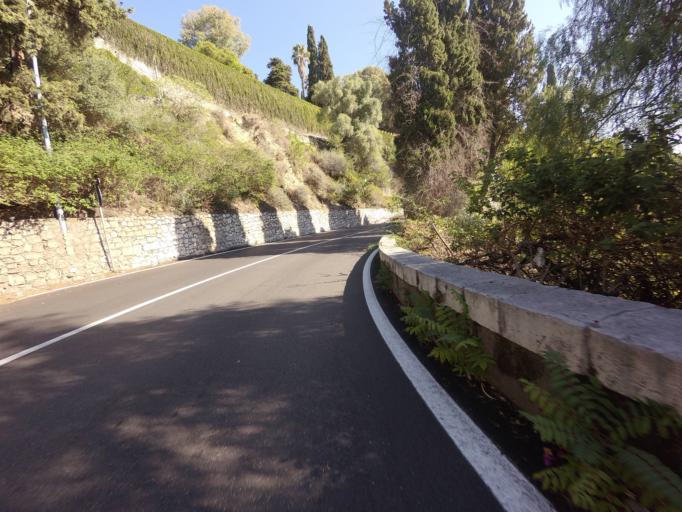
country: IT
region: Sicily
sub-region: Messina
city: Taormina
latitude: 37.8492
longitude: 15.2917
